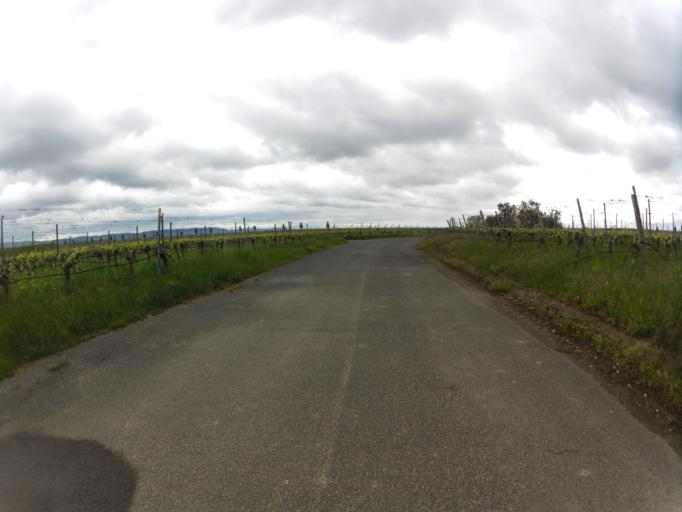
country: DE
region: Bavaria
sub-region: Regierungsbezirk Unterfranken
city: Sommerach
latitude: 49.8398
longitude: 10.2106
